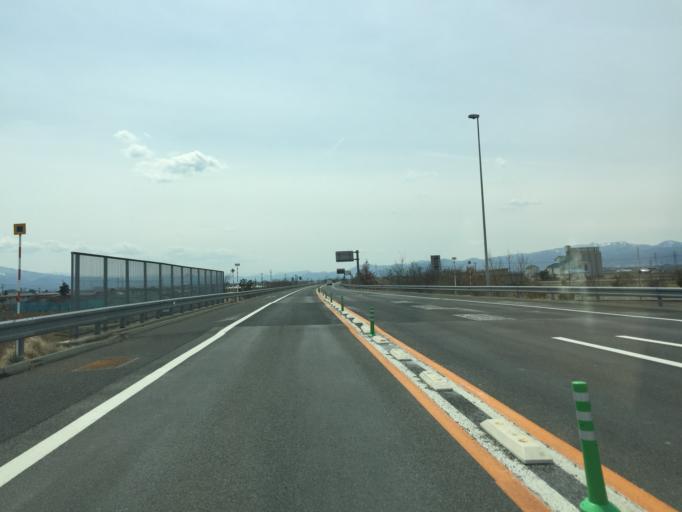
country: JP
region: Yamagata
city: Tendo
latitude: 38.3613
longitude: 140.3451
